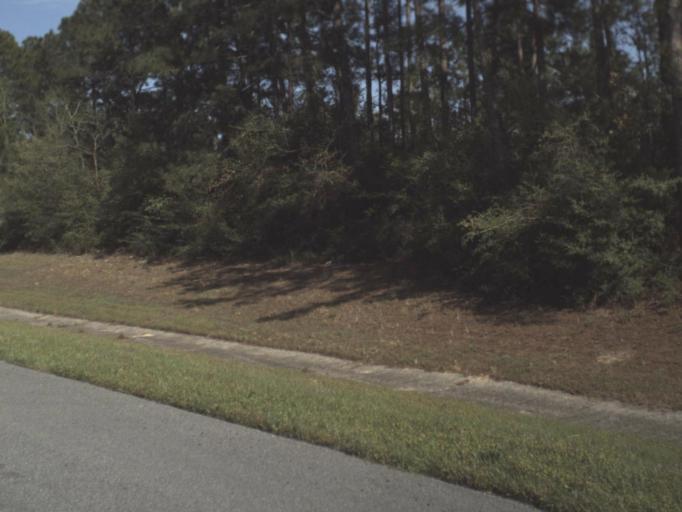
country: US
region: Florida
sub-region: Okaloosa County
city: Crestview
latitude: 30.7232
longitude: -86.5916
